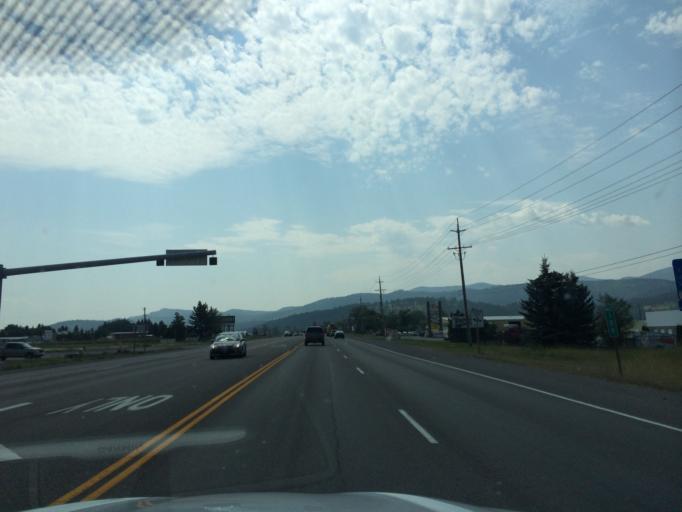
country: US
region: Montana
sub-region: Flathead County
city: Kalispell
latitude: 48.1543
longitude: -114.2878
